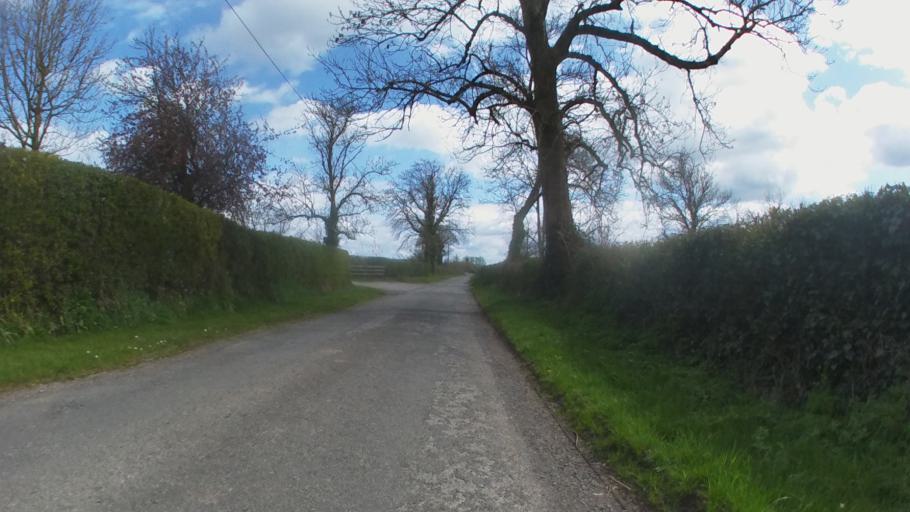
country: IE
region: Leinster
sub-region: Kilkenny
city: Kilkenny
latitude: 52.7087
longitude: -7.2153
